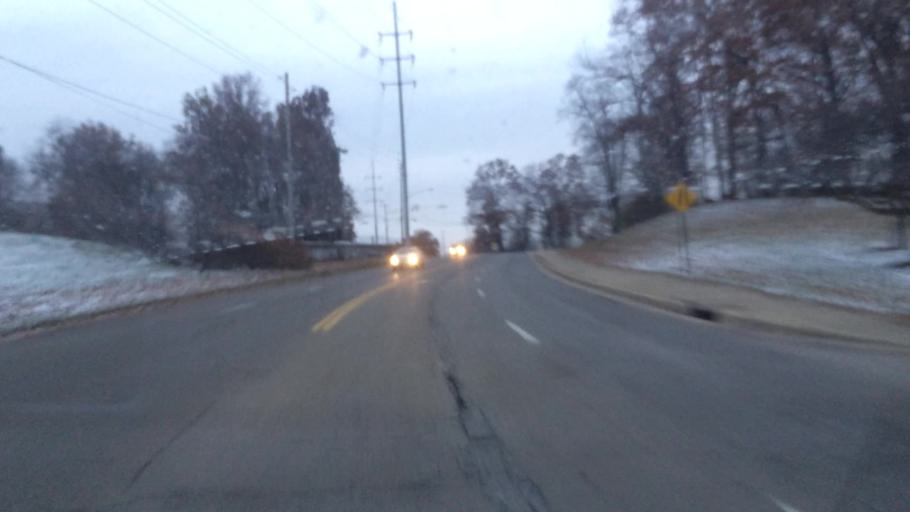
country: US
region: Ohio
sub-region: Summit County
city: Akron
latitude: 41.0596
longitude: -81.5405
